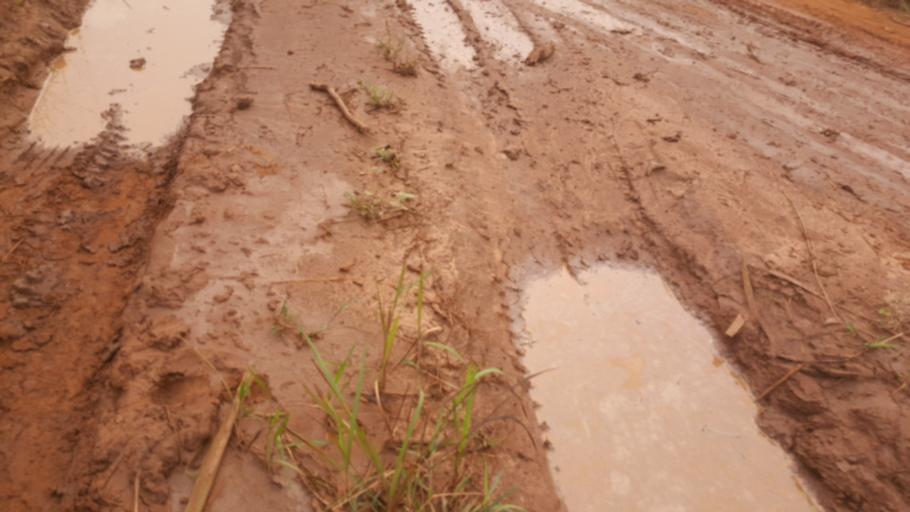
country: CD
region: Bandundu
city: Bandundu
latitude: -3.4666
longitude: 17.7147
